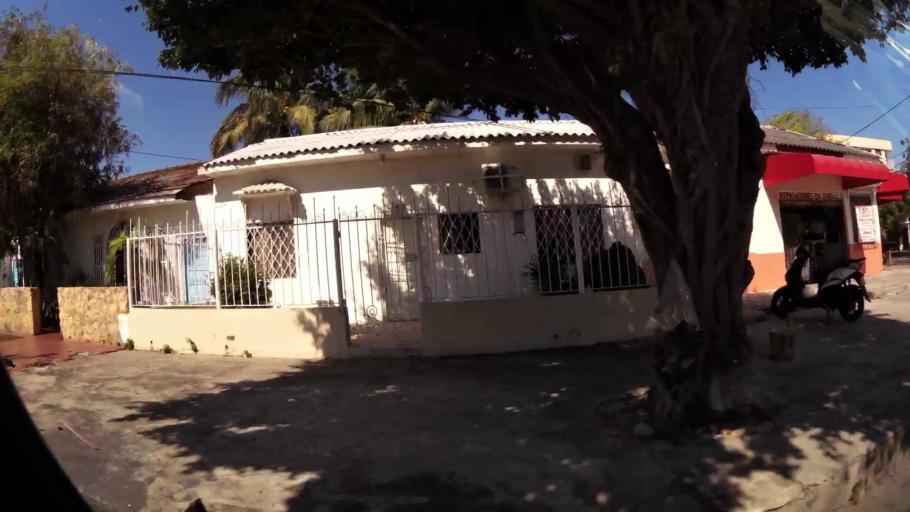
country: CO
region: Atlantico
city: Barranquilla
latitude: 10.9917
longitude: -74.8014
